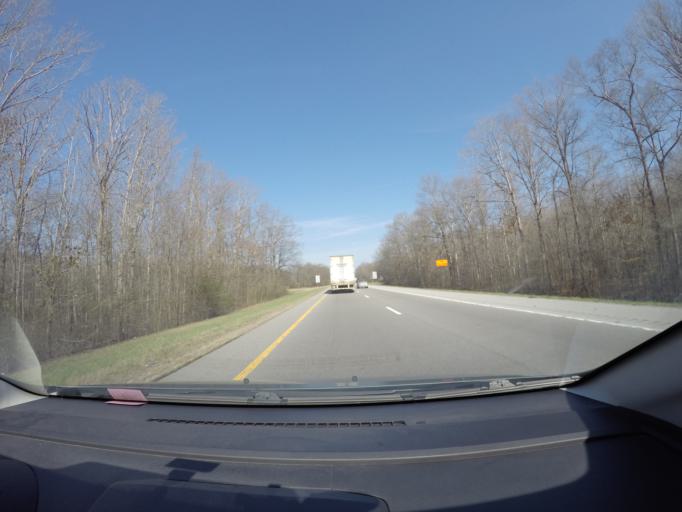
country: US
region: Tennessee
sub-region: Coffee County
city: Manchester
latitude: 35.4433
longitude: -86.0421
